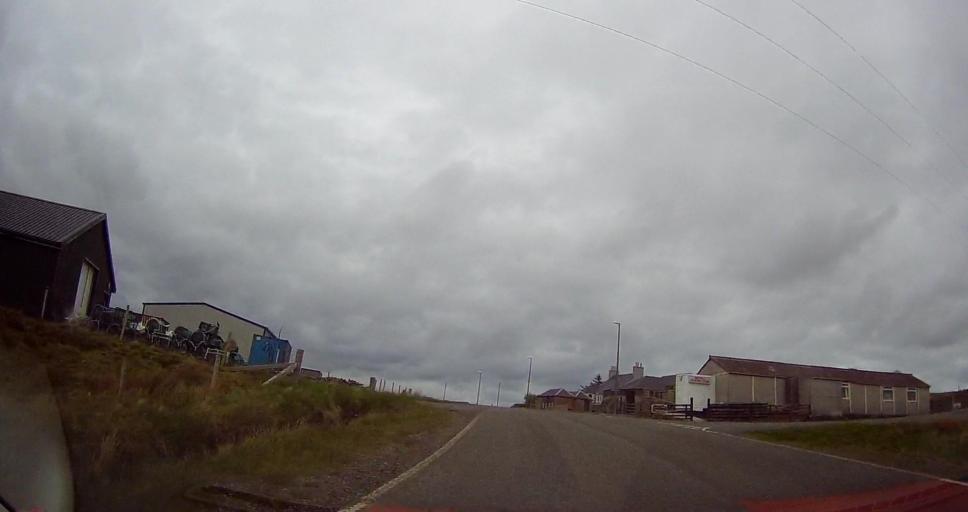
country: GB
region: Scotland
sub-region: Shetland Islands
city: Shetland
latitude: 60.5995
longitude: -1.0780
